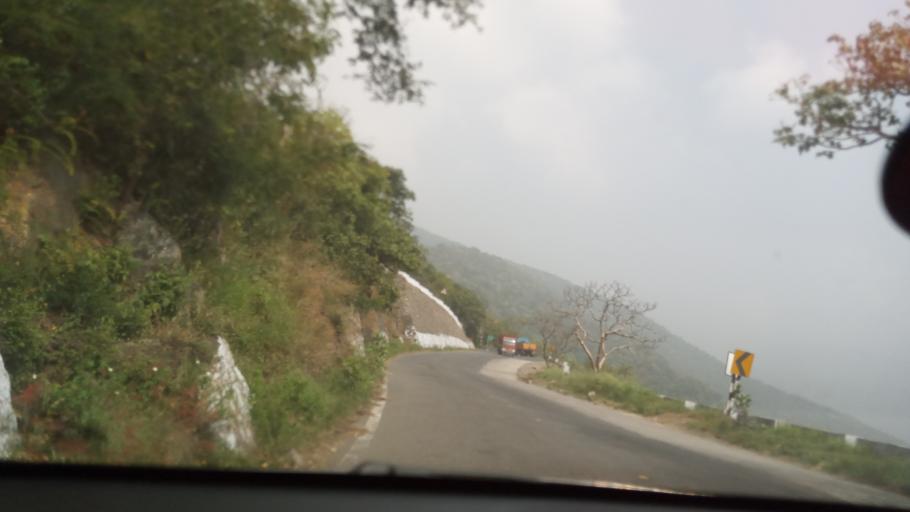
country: IN
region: Tamil Nadu
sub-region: Erode
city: Sathyamangalam
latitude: 11.5917
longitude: 77.1275
